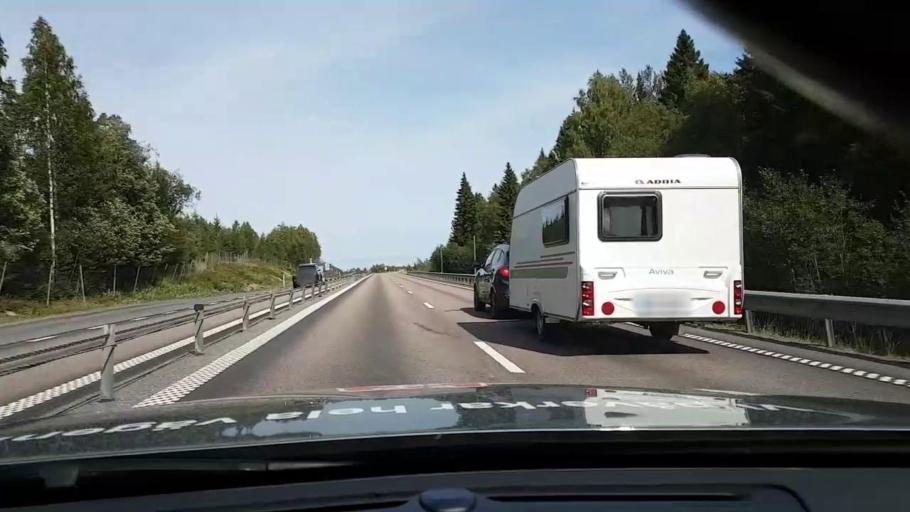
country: SE
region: Vaesternorrland
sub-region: OErnskoeldsviks Kommun
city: Husum
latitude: 63.3639
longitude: 19.1805
